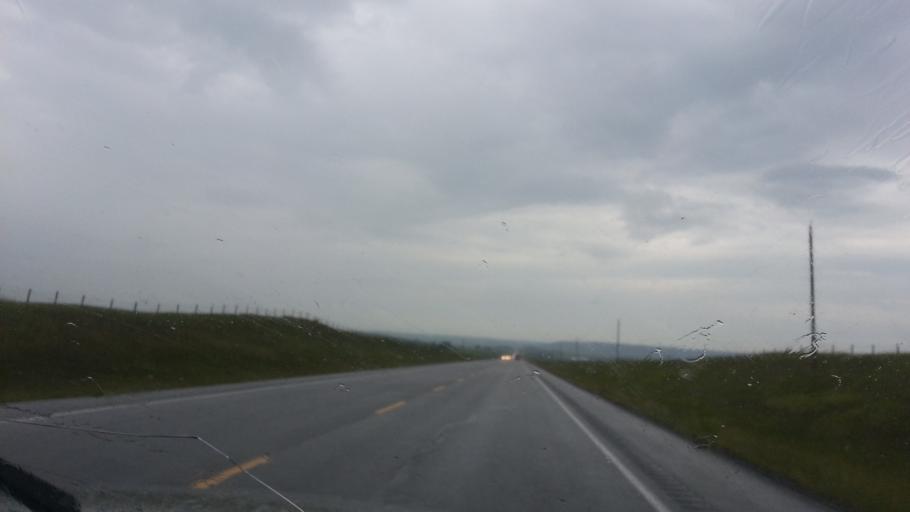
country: CA
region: Alberta
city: Cochrane
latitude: 51.1082
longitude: -114.4668
